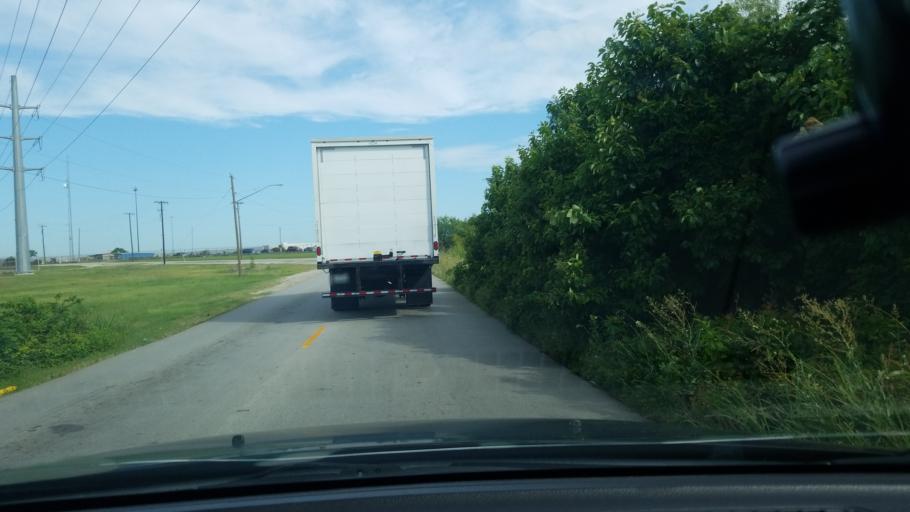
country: US
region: Texas
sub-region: Dallas County
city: Balch Springs
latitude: 32.7773
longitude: -96.6606
